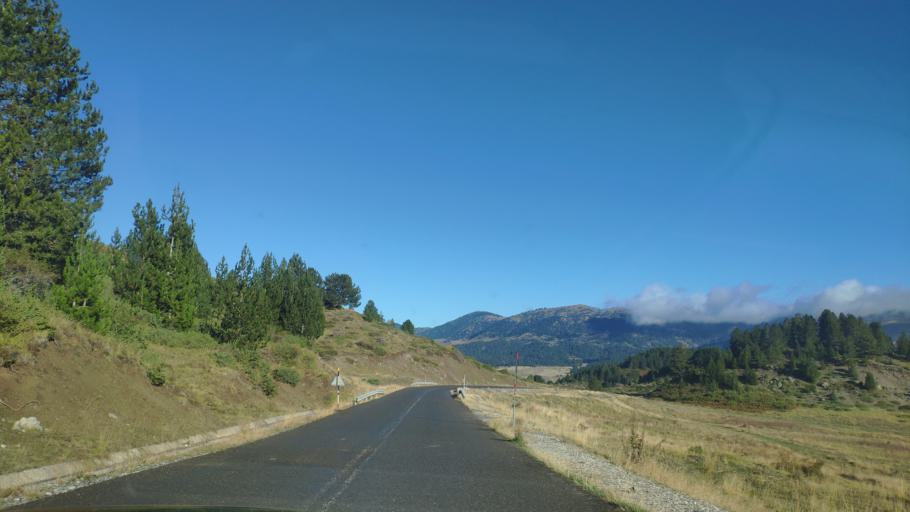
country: GR
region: Epirus
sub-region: Nomos Ioanninon
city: Metsovo
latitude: 39.7999
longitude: 21.1757
